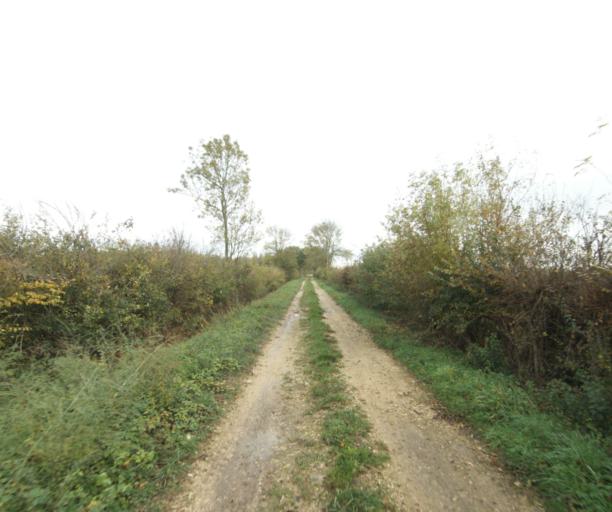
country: FR
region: Rhone-Alpes
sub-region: Departement de l'Ain
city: Pont-de-Vaux
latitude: 46.4529
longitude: 4.8945
